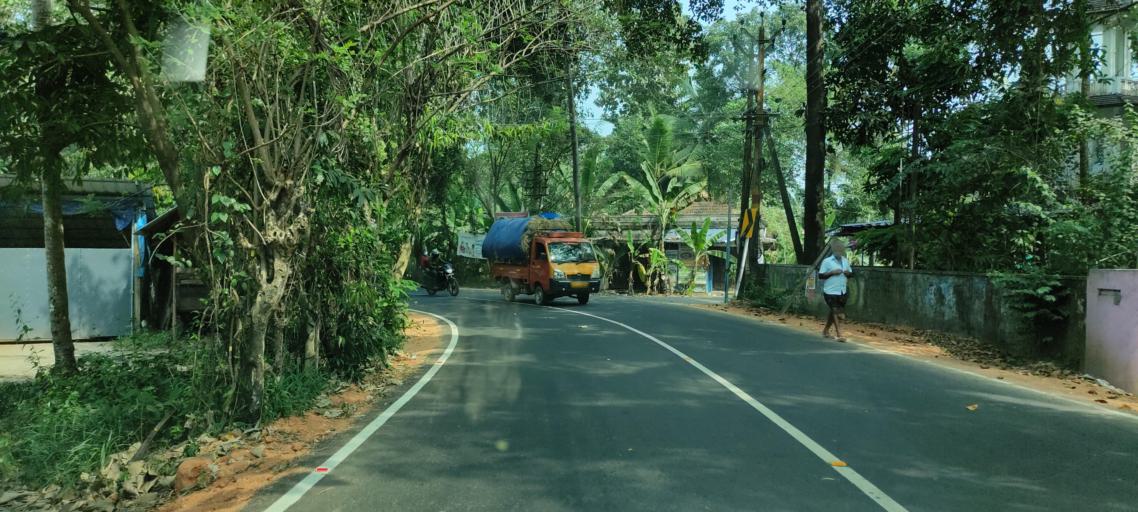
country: IN
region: Kerala
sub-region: Alappuzha
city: Shertallai
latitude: 9.6720
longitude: 76.3897
